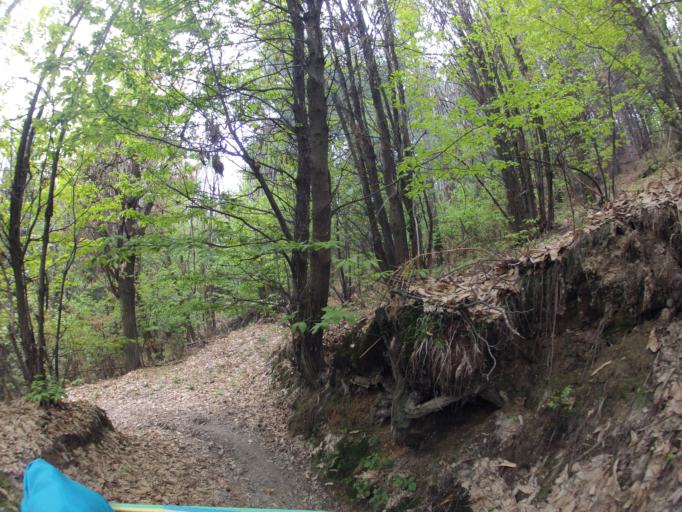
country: IT
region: Piedmont
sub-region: Provincia di Cuneo
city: Peveragno
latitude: 44.3278
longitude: 7.5958
